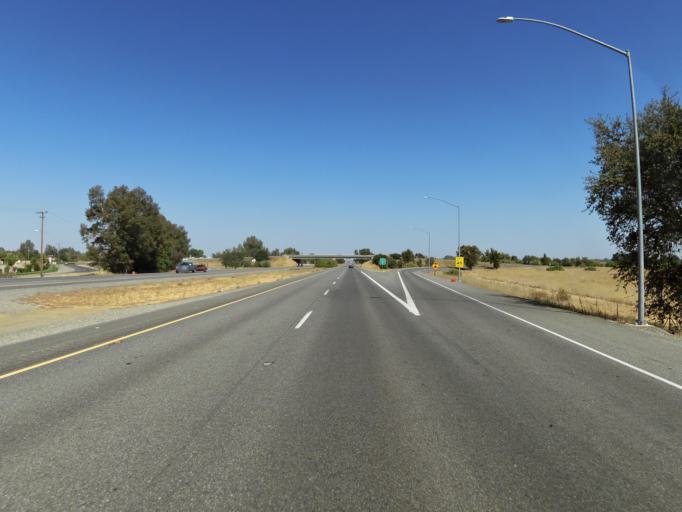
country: US
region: California
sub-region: Tehama County
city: Corning
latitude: 39.8785
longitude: -122.1999
